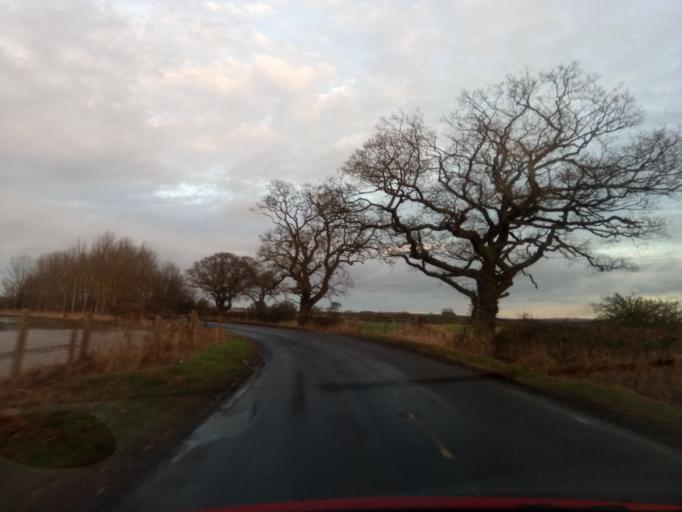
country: GB
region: England
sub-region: Northumberland
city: Ponteland
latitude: 55.0968
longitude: -1.7513
